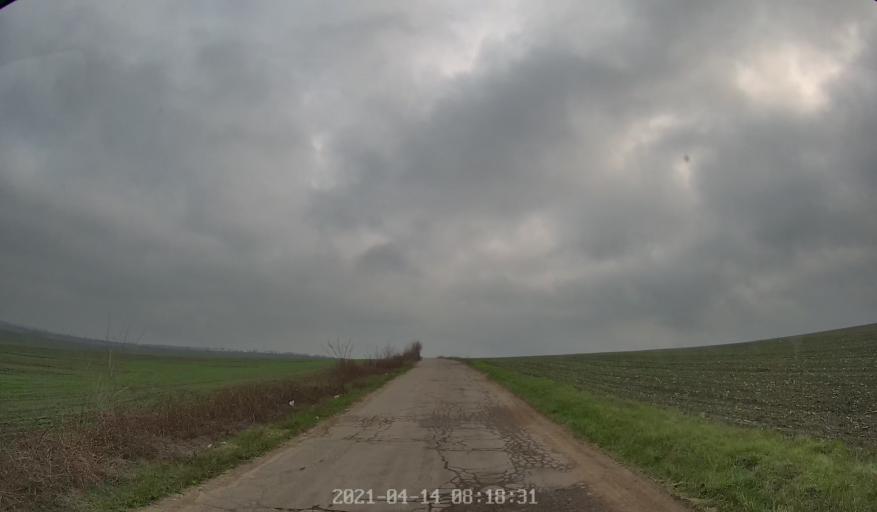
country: MD
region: Chisinau
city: Stauceni
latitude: 47.0562
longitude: 28.9173
